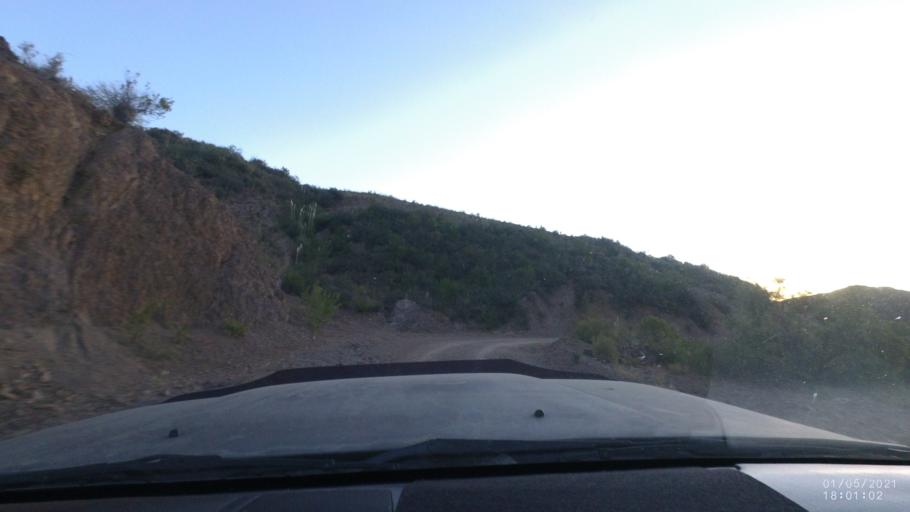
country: BO
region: Cochabamba
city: Capinota
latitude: -17.6852
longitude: -66.1697
